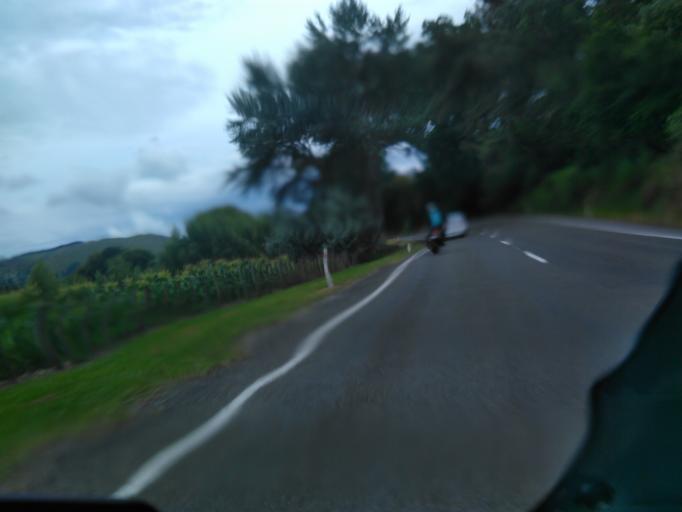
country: NZ
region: Gisborne
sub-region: Gisborne District
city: Gisborne
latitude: -38.4691
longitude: 177.8242
